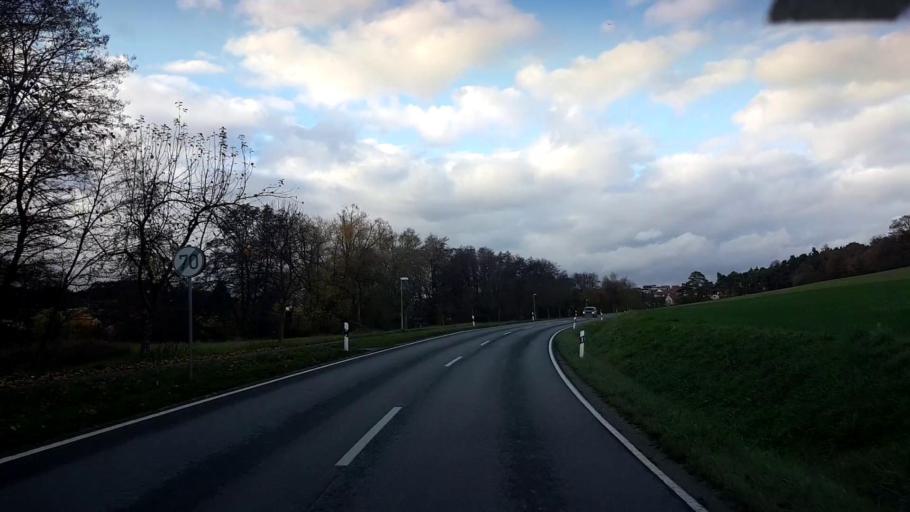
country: DE
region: Bavaria
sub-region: Upper Franconia
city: Priesendorf
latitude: 49.8985
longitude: 10.7179
